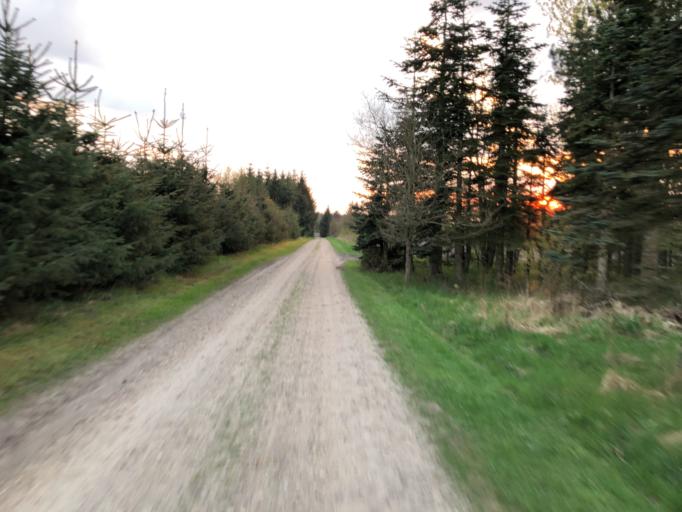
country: DK
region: Central Jutland
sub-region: Holstebro Kommune
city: Ulfborg
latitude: 56.2249
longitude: 8.4170
